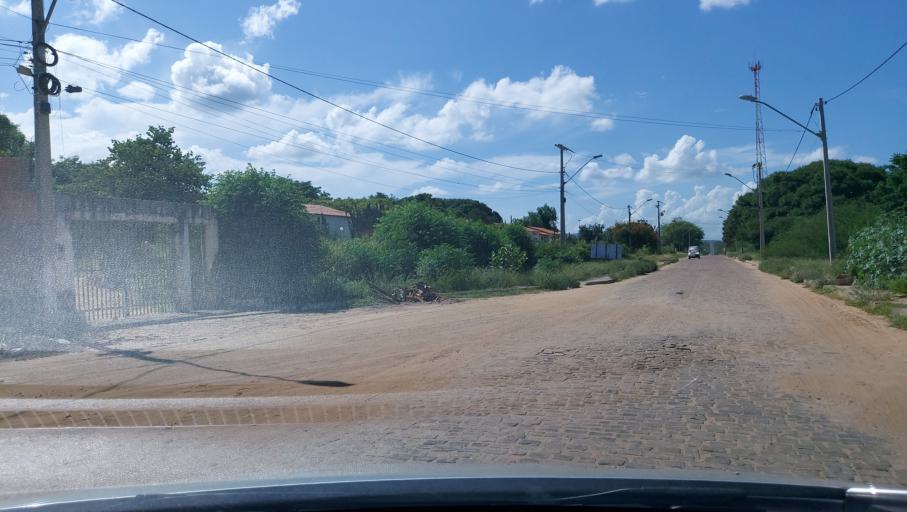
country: BR
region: Bahia
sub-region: Oliveira Dos Brejinhos
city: Beira Rio
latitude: -11.9960
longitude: -42.6288
